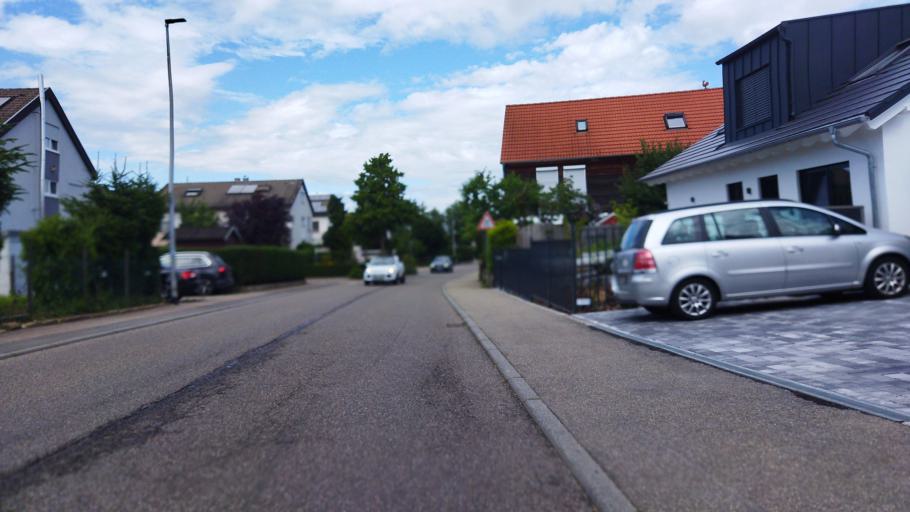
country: DE
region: Baden-Wuerttemberg
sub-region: Regierungsbezirk Stuttgart
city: Erligheim
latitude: 49.0214
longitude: 9.0996
